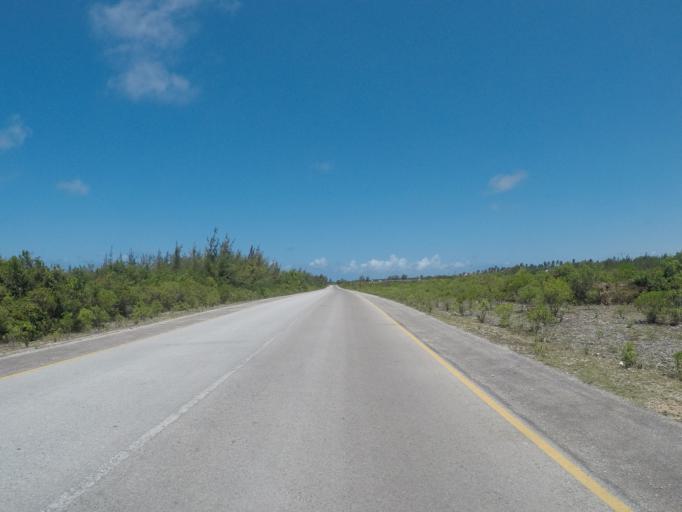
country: TZ
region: Zanzibar Central/South
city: Nganane
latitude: -6.4035
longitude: 39.5622
